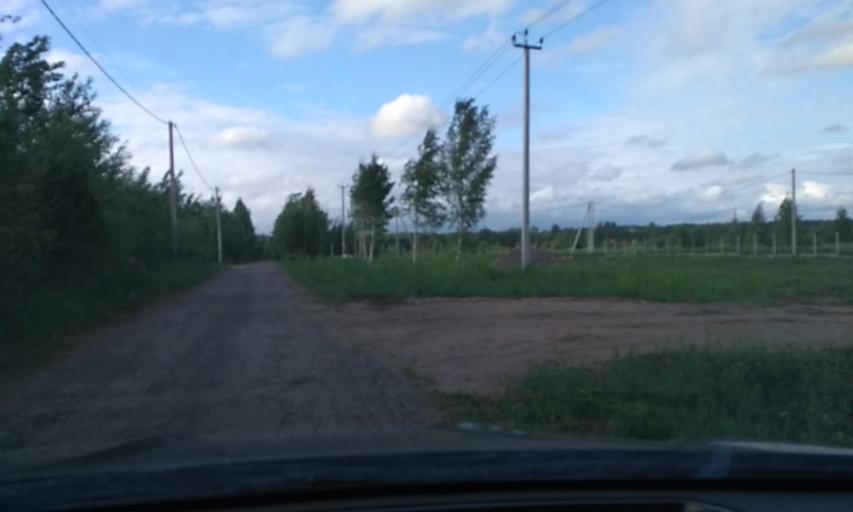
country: RU
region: Leningrad
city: Otradnoye
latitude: 59.8082
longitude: 30.8269
